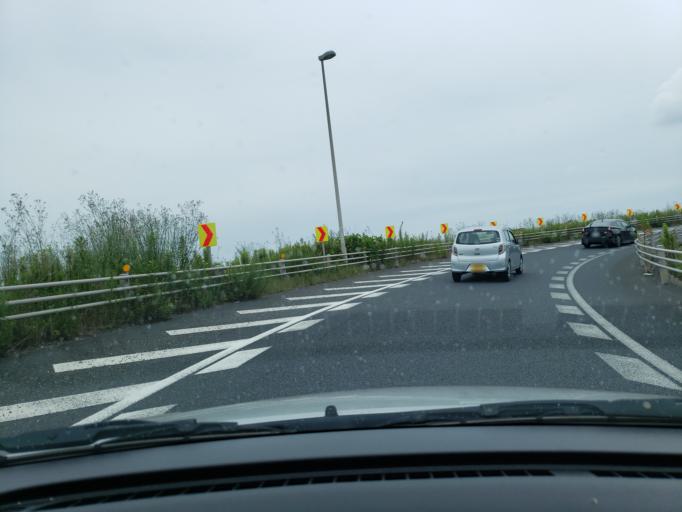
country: JP
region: Hyogo
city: Ono
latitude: 34.7804
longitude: 134.9042
